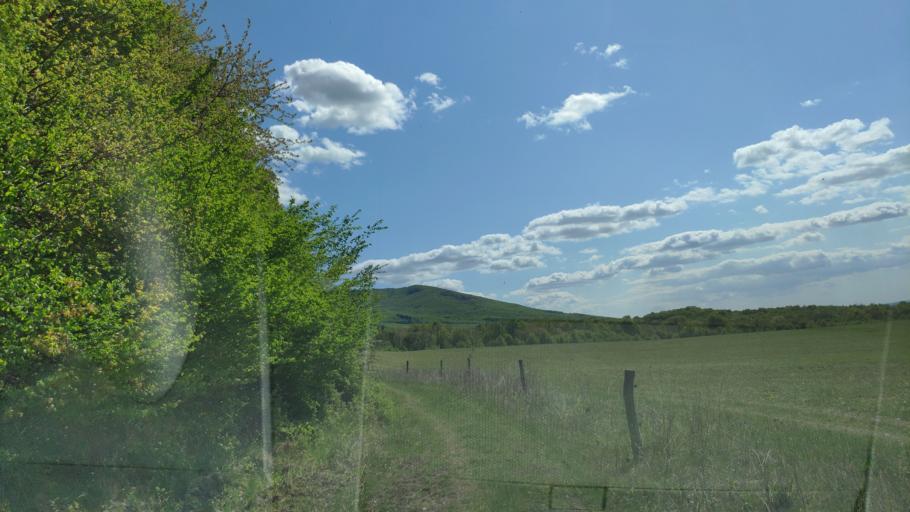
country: SK
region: Kosicky
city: Kosice
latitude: 48.6568
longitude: 21.4300
